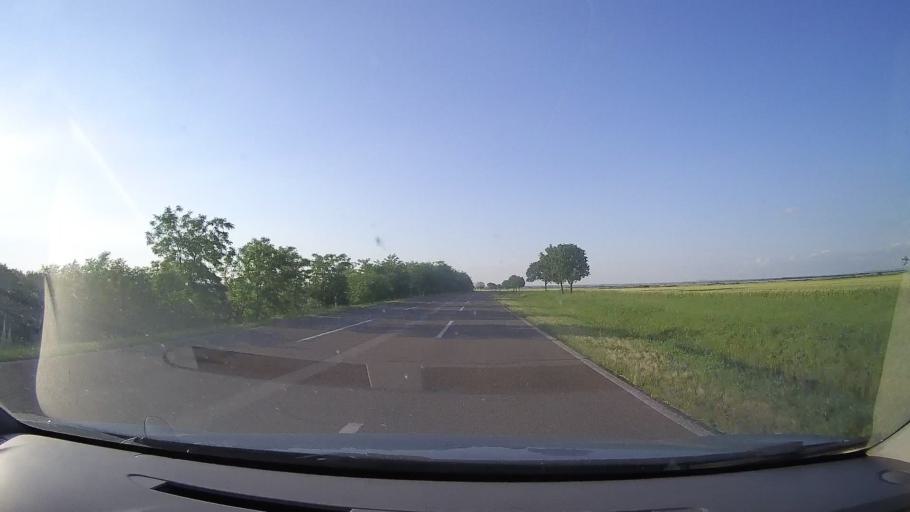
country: RO
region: Timis
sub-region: Comuna Moravita
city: Moravita
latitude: 45.2139
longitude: 21.2997
